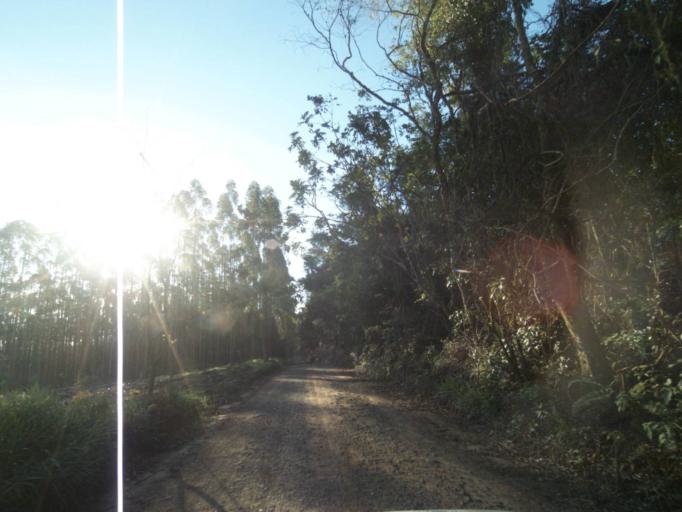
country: BR
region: Parana
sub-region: Telemaco Borba
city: Telemaco Borba
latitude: -24.4994
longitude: -50.5986
